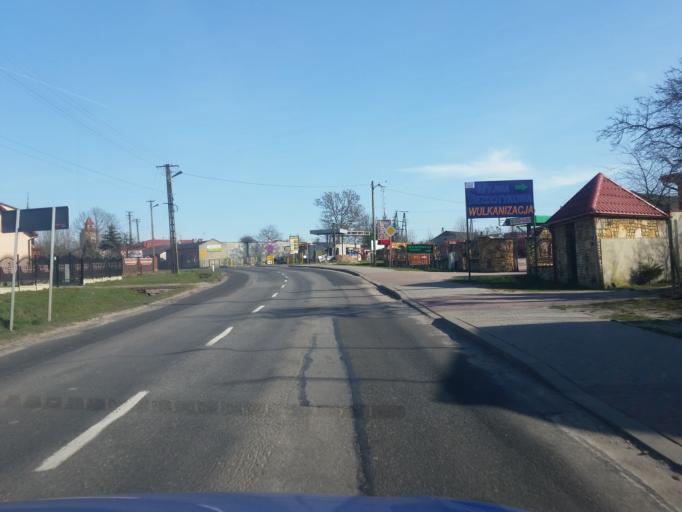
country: PL
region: Lodz Voivodeship
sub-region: Powiat radomszczanski
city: Kamiensk
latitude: 51.2061
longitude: 19.4937
